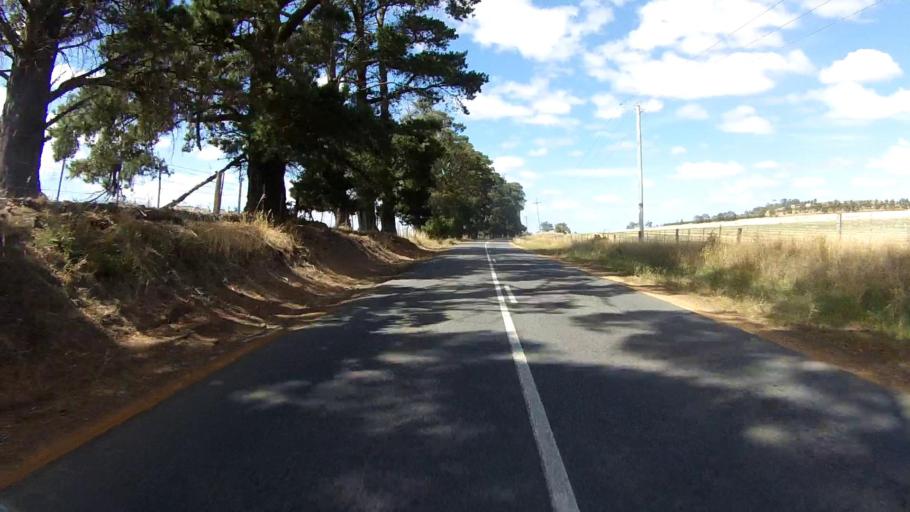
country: AU
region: Tasmania
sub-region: Sorell
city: Sorell
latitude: -42.6382
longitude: 147.4327
